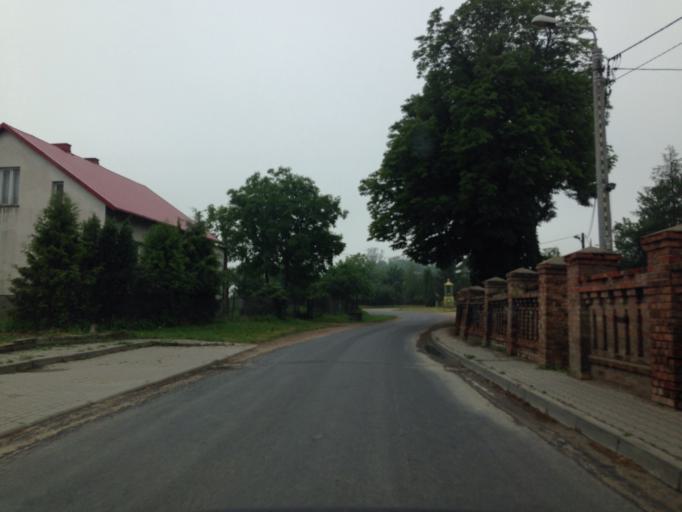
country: PL
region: Kujawsko-Pomorskie
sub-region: Powiat brodnicki
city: Bobrowo
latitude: 53.3265
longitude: 19.3151
